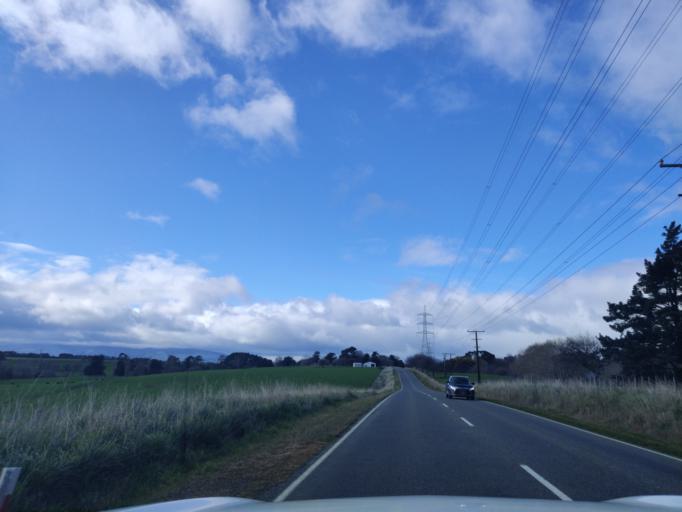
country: NZ
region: Manawatu-Wanganui
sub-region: Palmerston North City
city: Palmerston North
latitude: -40.2838
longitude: 175.6544
